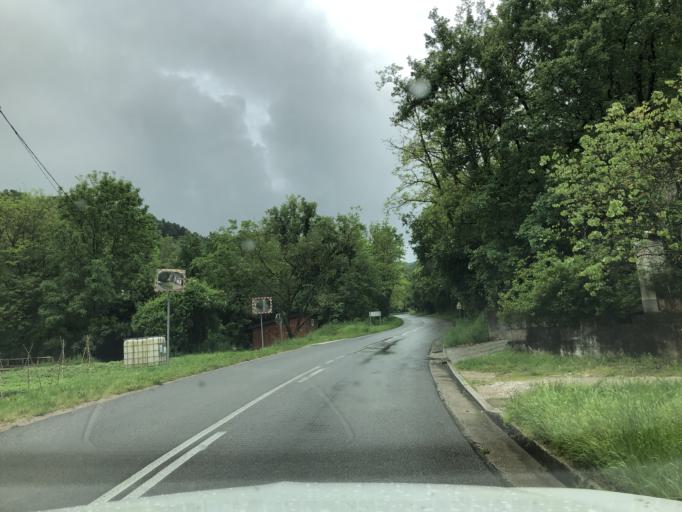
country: SI
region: Koper-Capodistria
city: Prade
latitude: 45.5160
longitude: 13.7800
